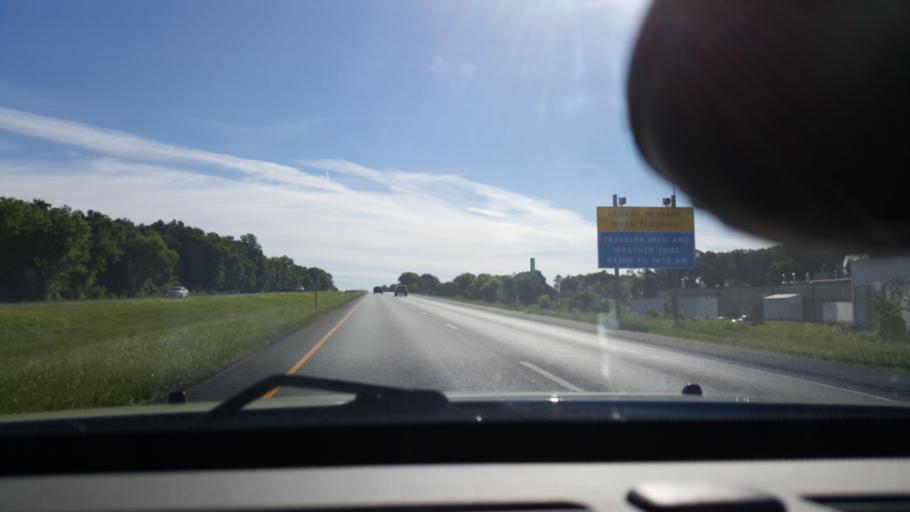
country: US
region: Pennsylvania
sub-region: York County
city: Yorklyn
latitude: 39.9940
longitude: -76.6547
